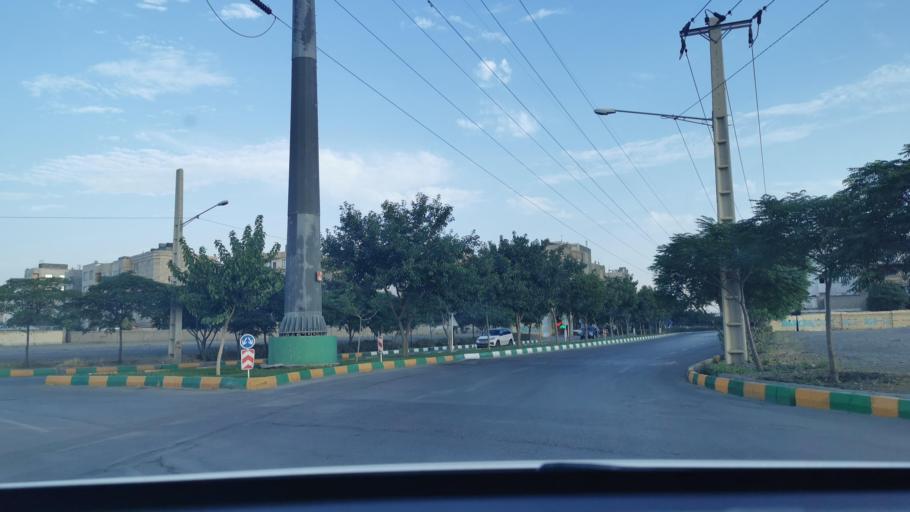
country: IR
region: Razavi Khorasan
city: Mashhad
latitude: 36.3502
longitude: 59.5311
